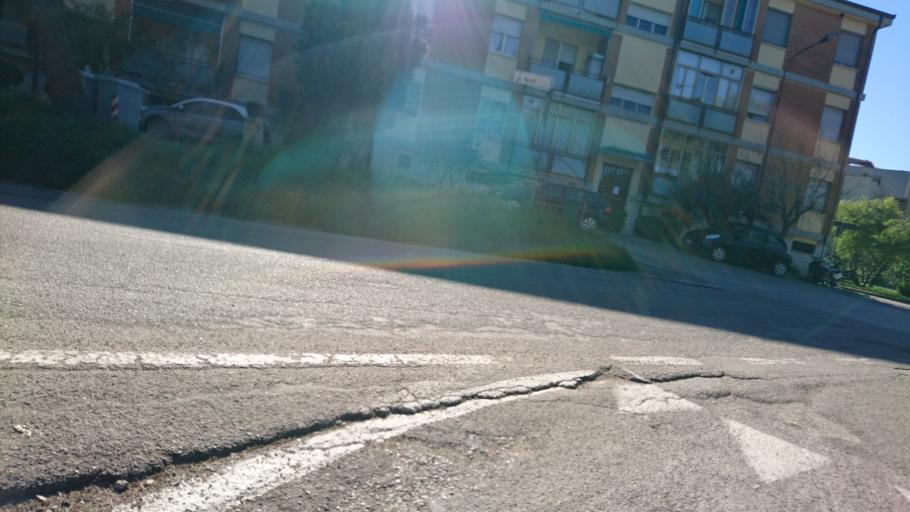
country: IT
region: The Marches
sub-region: Provincia di Pesaro e Urbino
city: Pesaro
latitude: 43.8994
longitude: 12.8934
